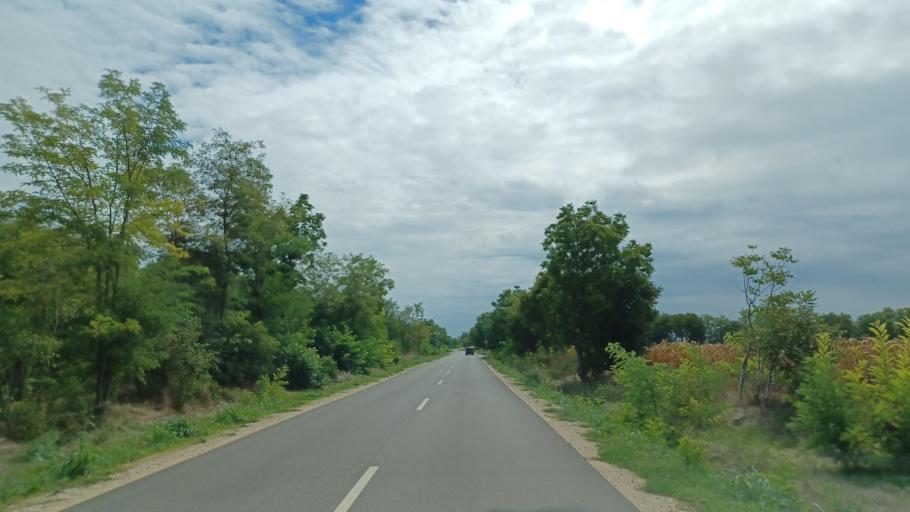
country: HU
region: Tolna
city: Zomba
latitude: 46.4553
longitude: 18.6008
